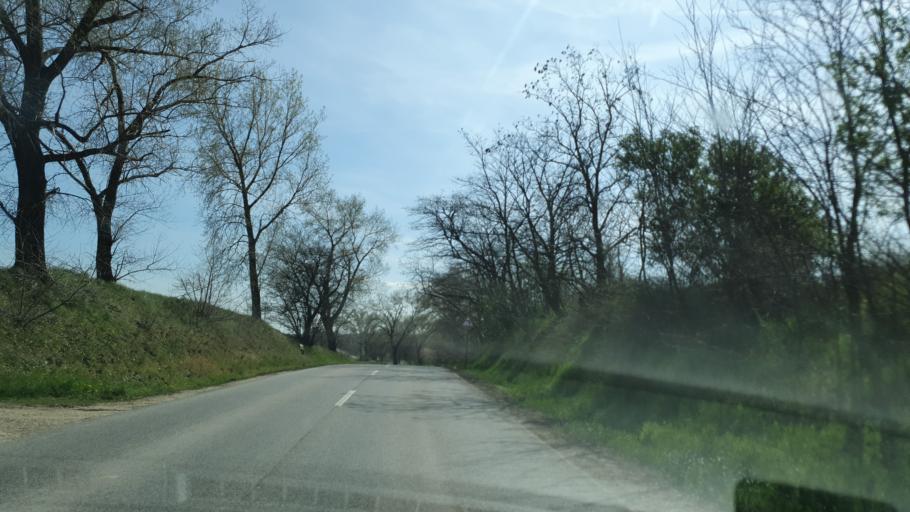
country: HU
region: Komarom-Esztergom
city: Bokod
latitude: 47.4880
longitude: 18.2417
